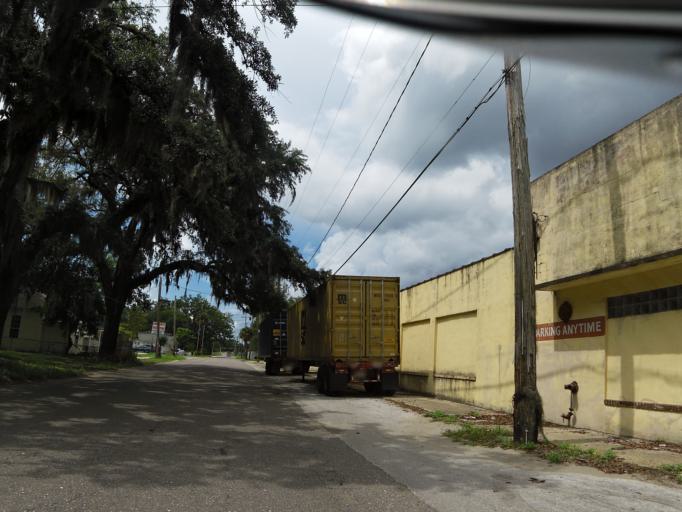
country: US
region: Florida
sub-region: Duval County
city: Jacksonville
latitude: 30.3733
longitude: -81.6400
